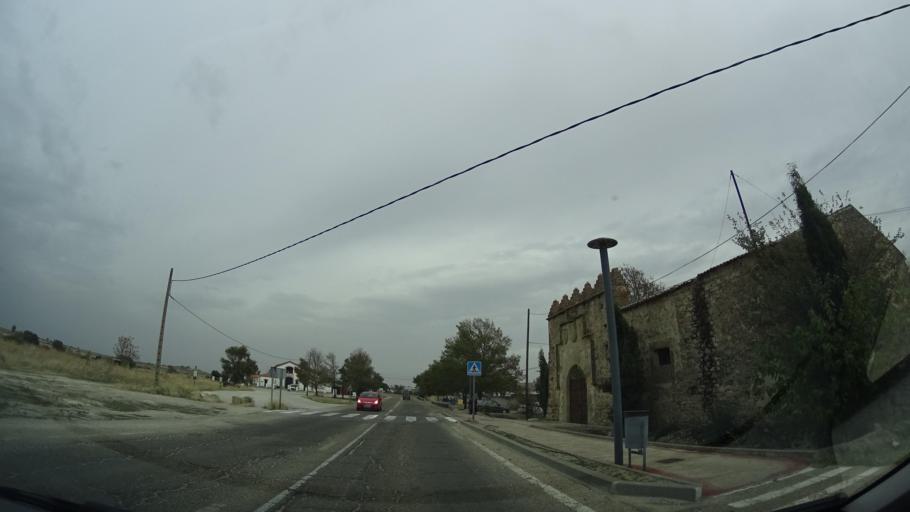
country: ES
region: Extremadura
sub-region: Provincia de Caceres
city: Trujillo
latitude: 39.4620
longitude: -5.8682
